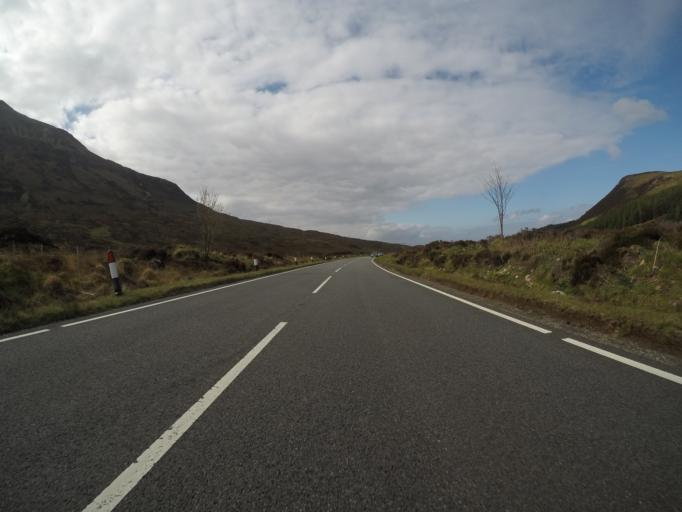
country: GB
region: Scotland
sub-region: Highland
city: Portree
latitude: 57.2986
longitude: -6.0889
